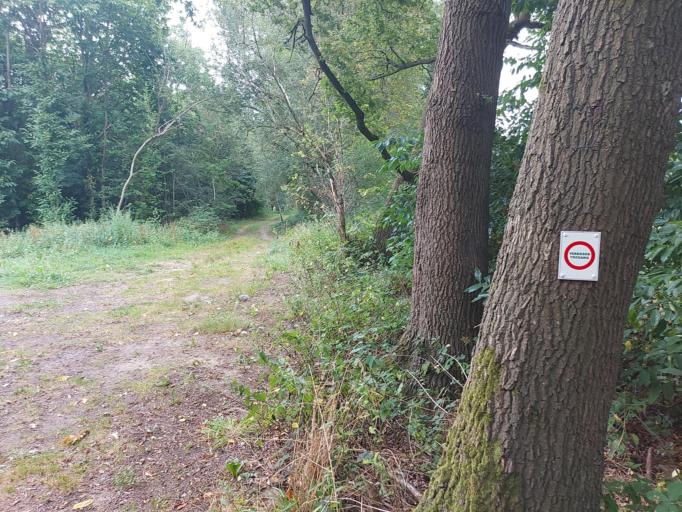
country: BE
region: Flanders
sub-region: Provincie Antwerpen
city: Olen
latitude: 51.1543
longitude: 4.8609
